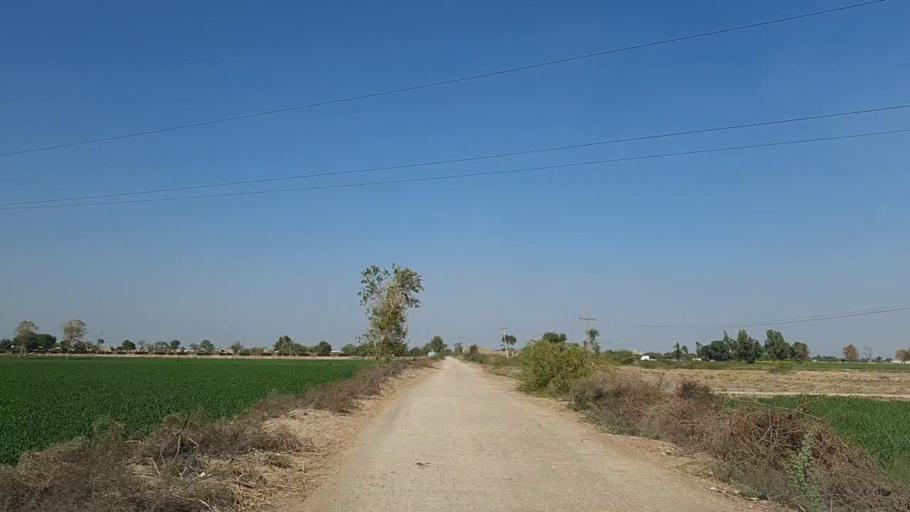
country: PK
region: Sindh
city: Nawabshah
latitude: 26.2512
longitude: 68.4411
